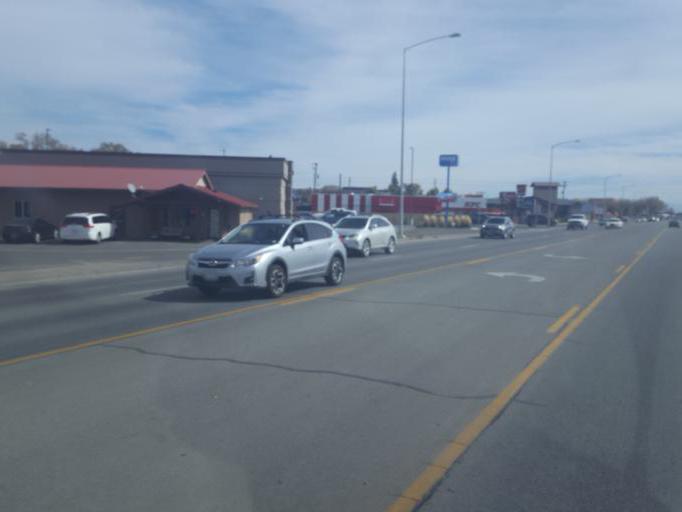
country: US
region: Colorado
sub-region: Alamosa County
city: Alamosa
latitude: 37.4721
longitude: -105.8876
